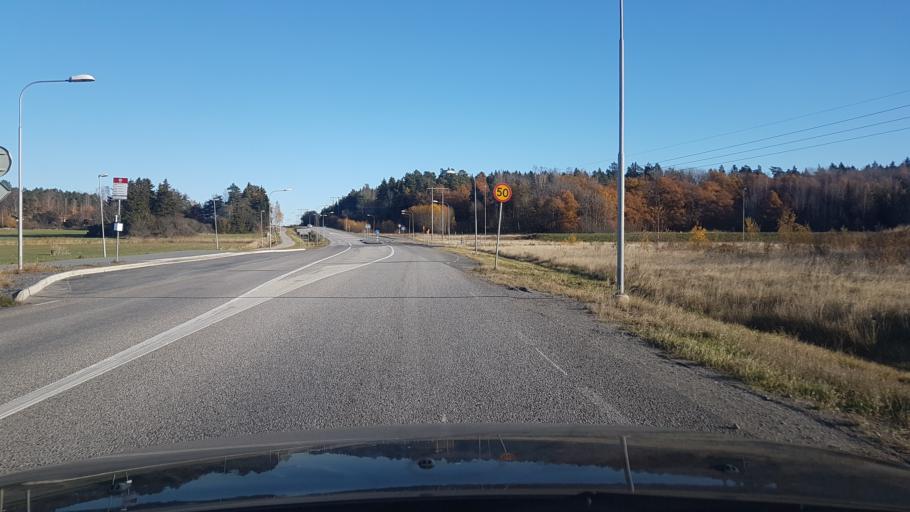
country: SE
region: Stockholm
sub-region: Sigtuna Kommun
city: Marsta
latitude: 59.6286
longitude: 17.8870
